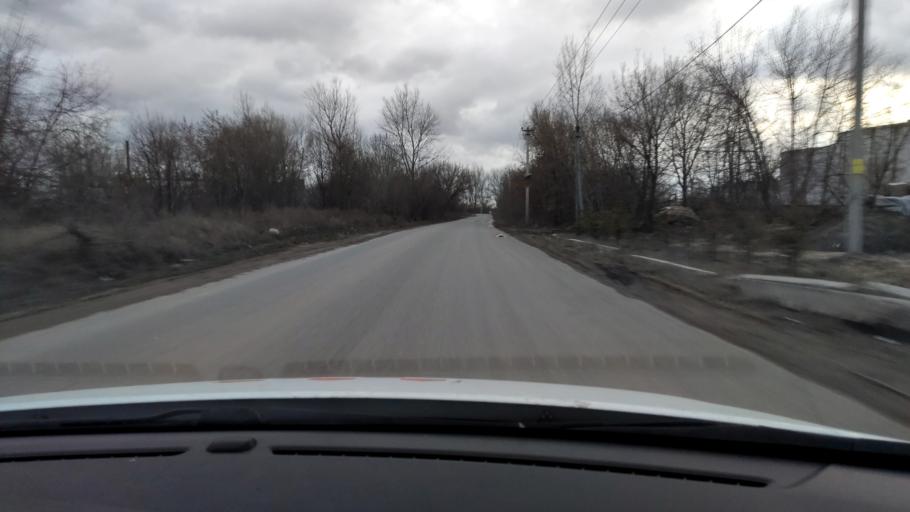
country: RU
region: Tatarstan
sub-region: Gorod Kazan'
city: Kazan
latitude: 55.7260
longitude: 49.0976
